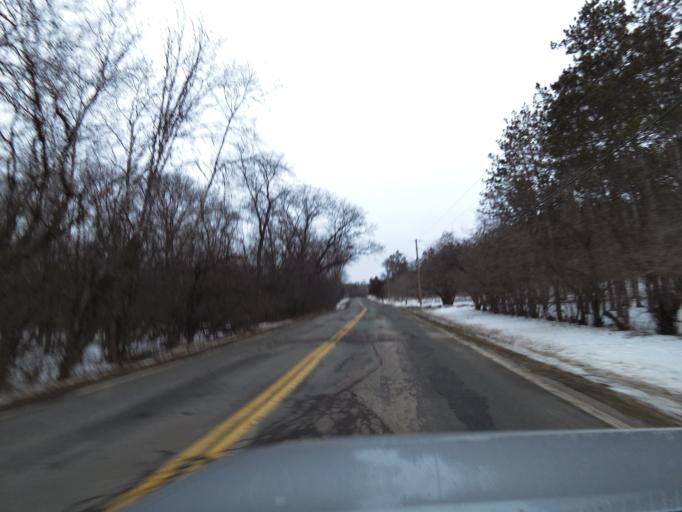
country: US
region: Minnesota
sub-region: Washington County
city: Afton
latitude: 44.8674
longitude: -92.8017
